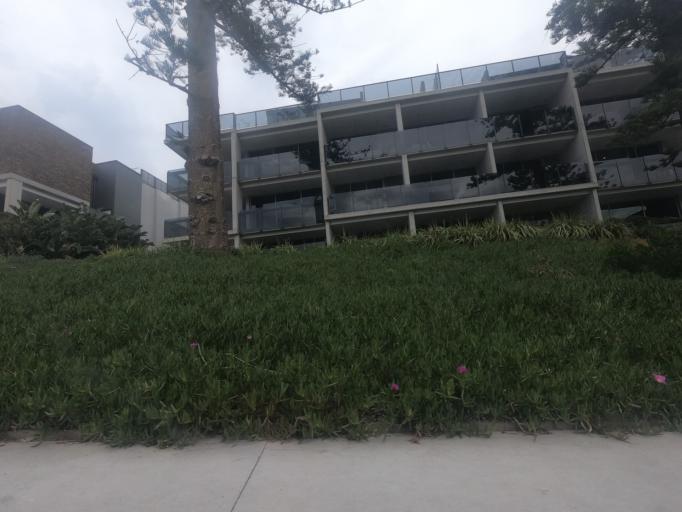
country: AU
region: New South Wales
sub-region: Wollongong
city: Bulli
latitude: -34.3011
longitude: 150.9405
